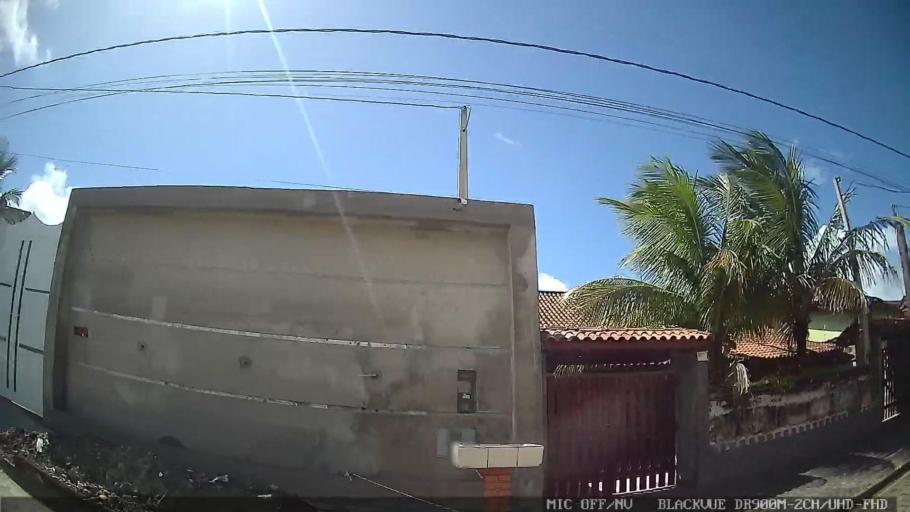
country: BR
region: Sao Paulo
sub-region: Itanhaem
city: Itanhaem
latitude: -24.2315
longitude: -46.8699
